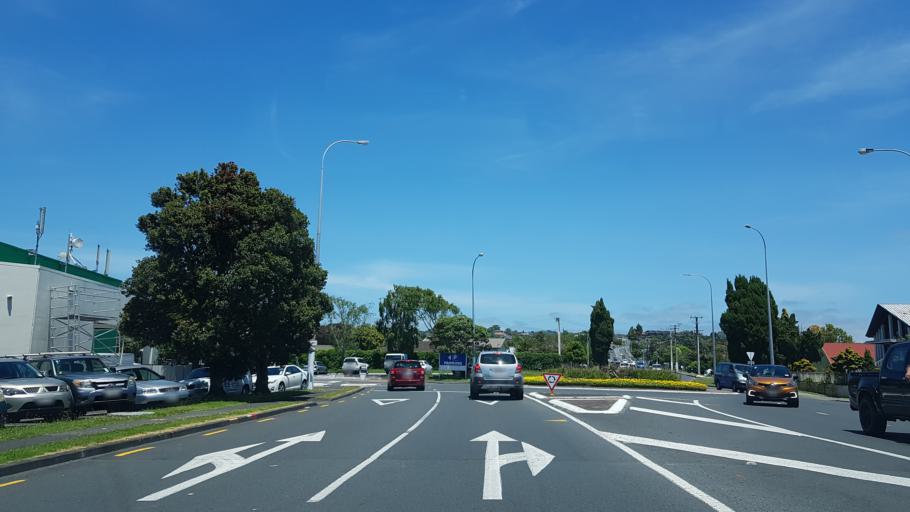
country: NZ
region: Auckland
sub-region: Auckland
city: Waitakere
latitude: -36.9091
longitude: 174.6631
